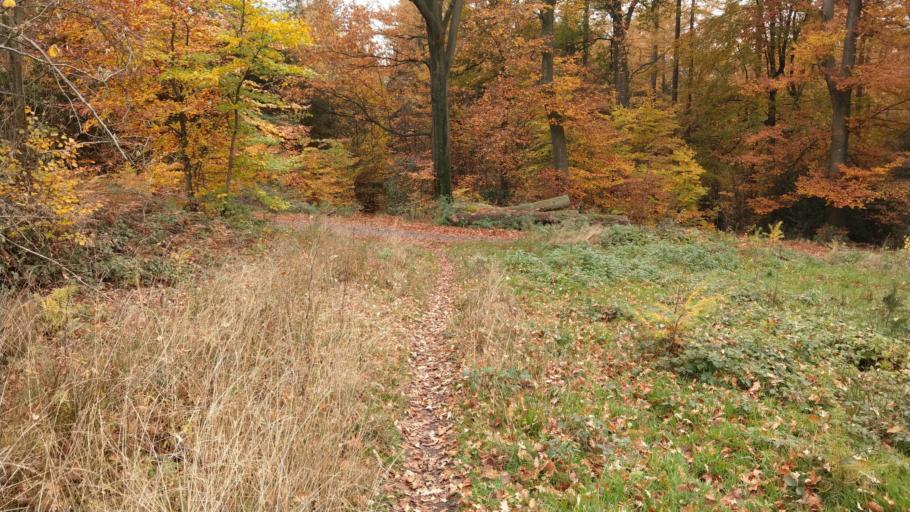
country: BE
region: Wallonia
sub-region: Province de Liege
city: La Calamine
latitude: 50.7386
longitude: 6.0132
